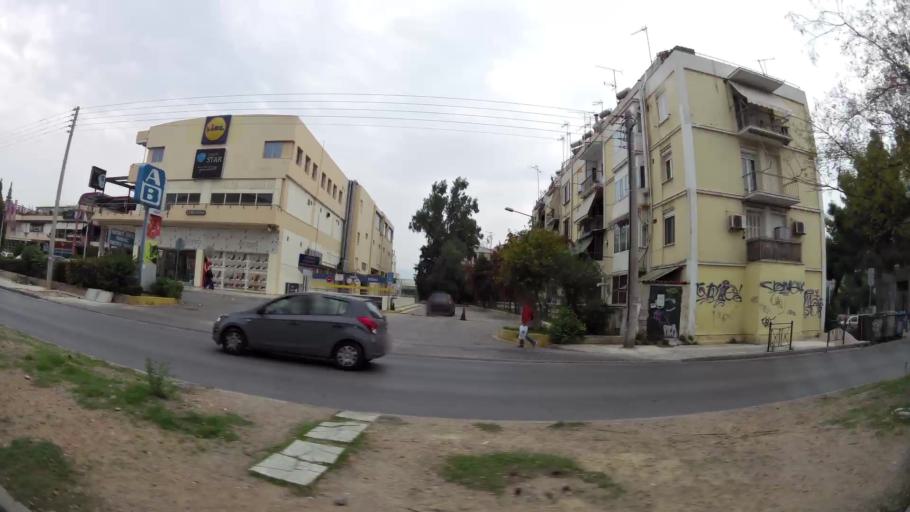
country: GR
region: Attica
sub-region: Nomos Piraios
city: Agios Ioannis Rentis
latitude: 37.9737
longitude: 23.6657
